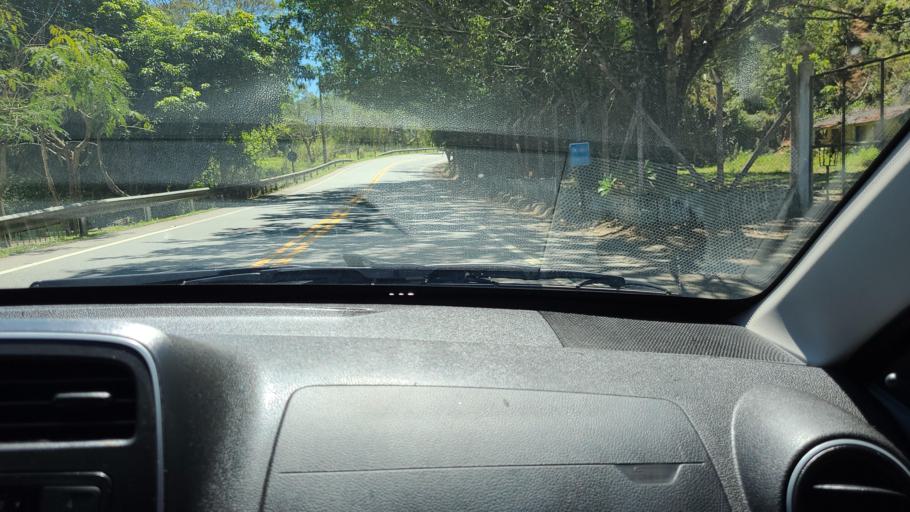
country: BR
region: Sao Paulo
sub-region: Tremembe
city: Tremembe
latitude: -22.8778
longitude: -45.5796
